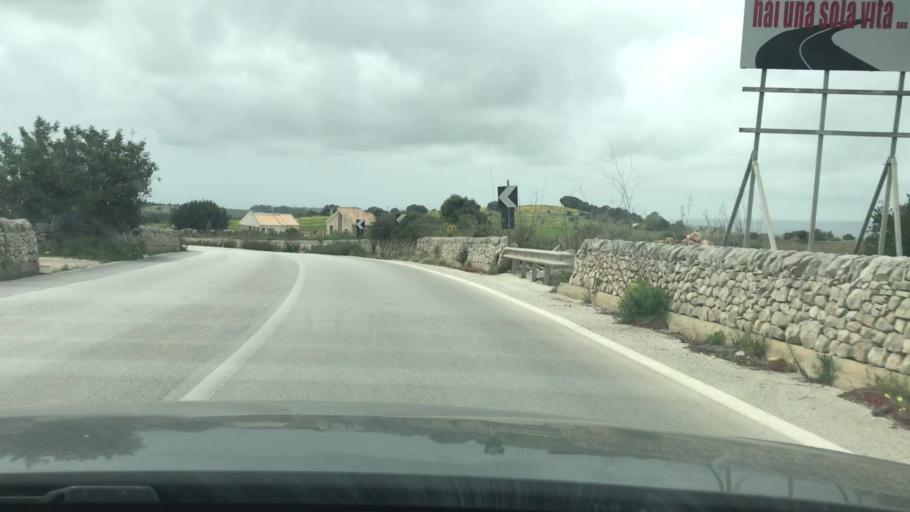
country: IT
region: Sicily
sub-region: Ragusa
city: Scicli
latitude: 36.8162
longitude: 14.7357
